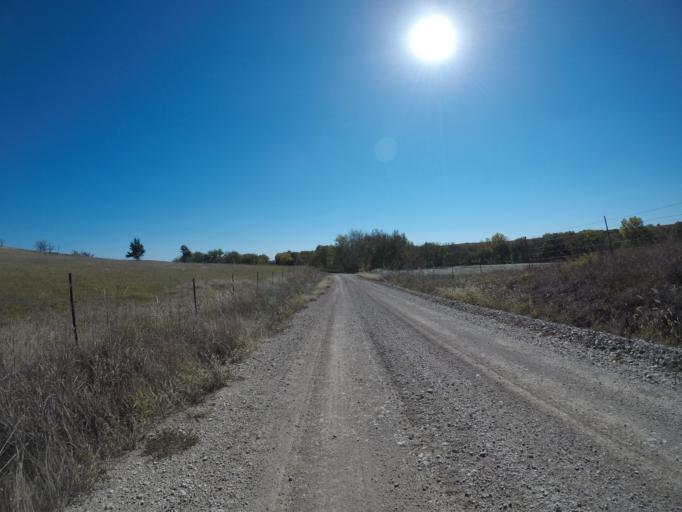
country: US
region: Kansas
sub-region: Wabaunsee County
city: Alma
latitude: 39.0151
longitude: -96.4092
